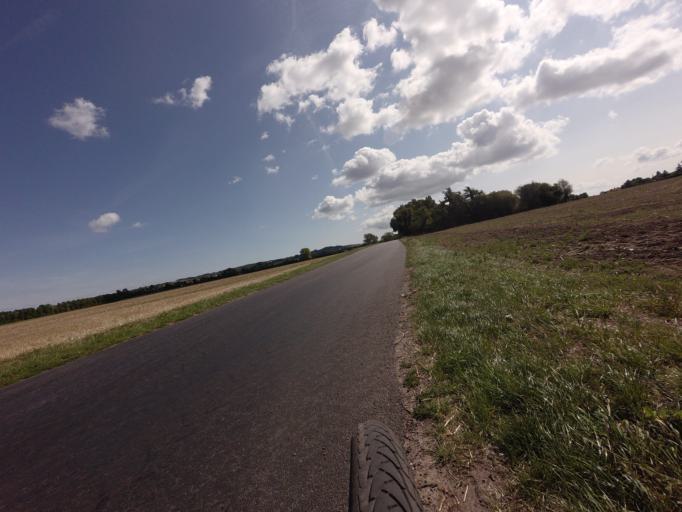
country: DK
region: Zealand
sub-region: Vordingborg Kommune
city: Stege
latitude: 54.9765
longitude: 12.4433
